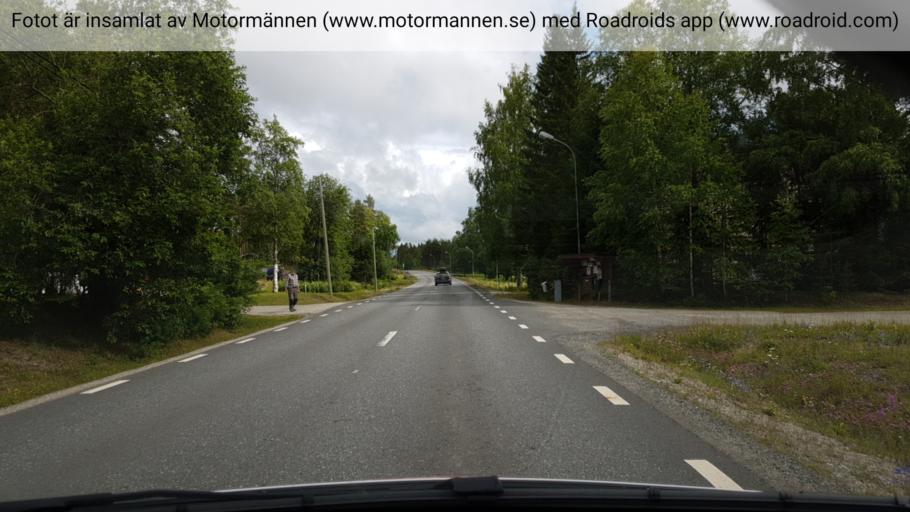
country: SE
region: Vaesterbotten
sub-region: Lycksele Kommun
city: Lycksele
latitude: 64.3970
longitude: 19.0515
